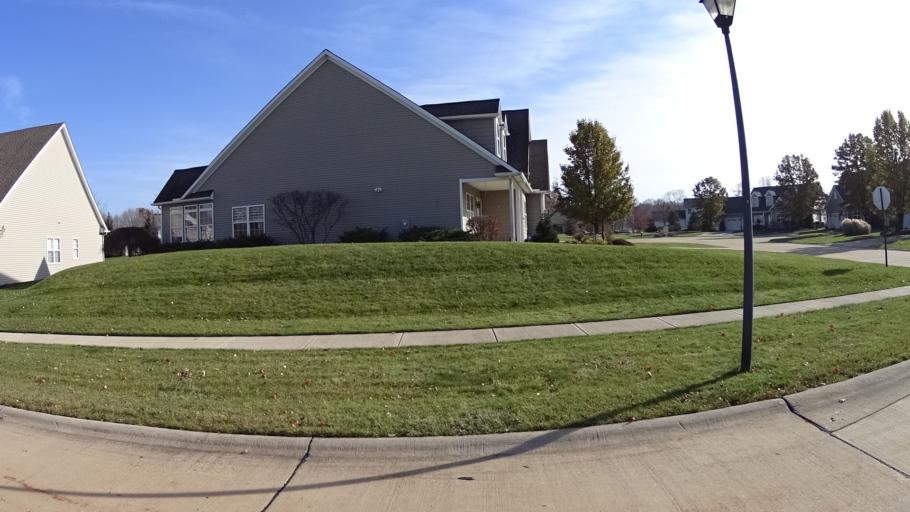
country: US
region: Ohio
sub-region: Lorain County
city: Avon
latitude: 41.4475
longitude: -82.0457
